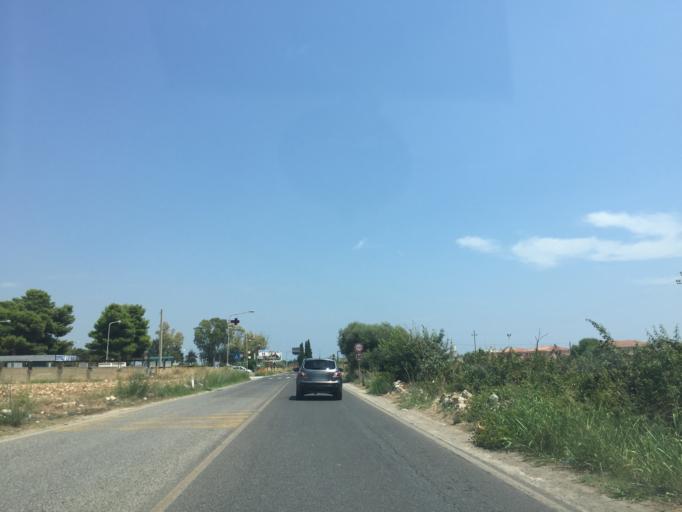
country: IT
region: Sicily
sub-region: Provincia di Siracusa
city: Avola
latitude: 36.9248
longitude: 15.1582
